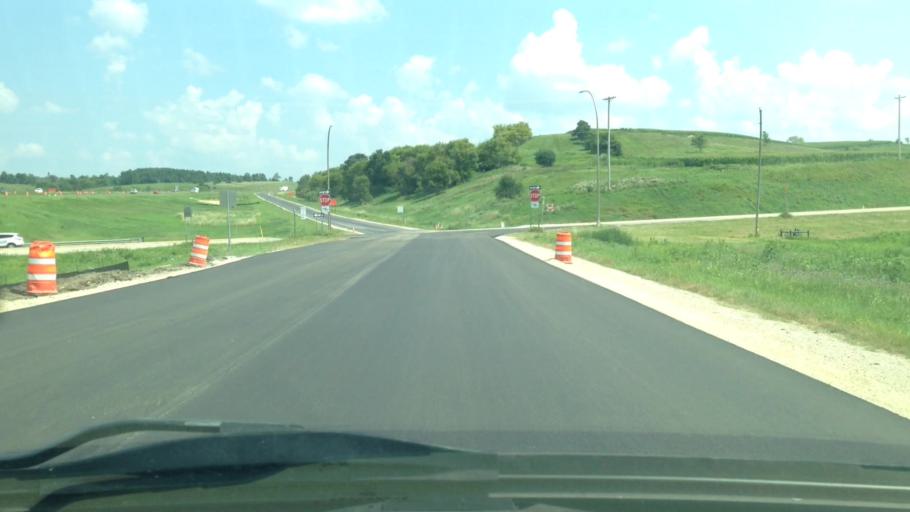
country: US
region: Minnesota
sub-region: Olmsted County
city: Rochester
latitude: 43.9736
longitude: -92.4401
